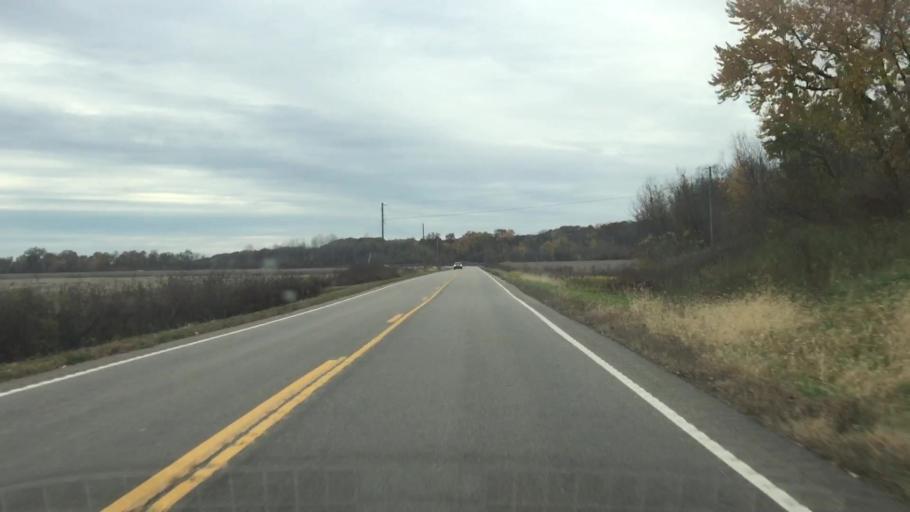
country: US
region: Missouri
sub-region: Callaway County
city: Fulton
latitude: 38.7078
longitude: -91.7491
